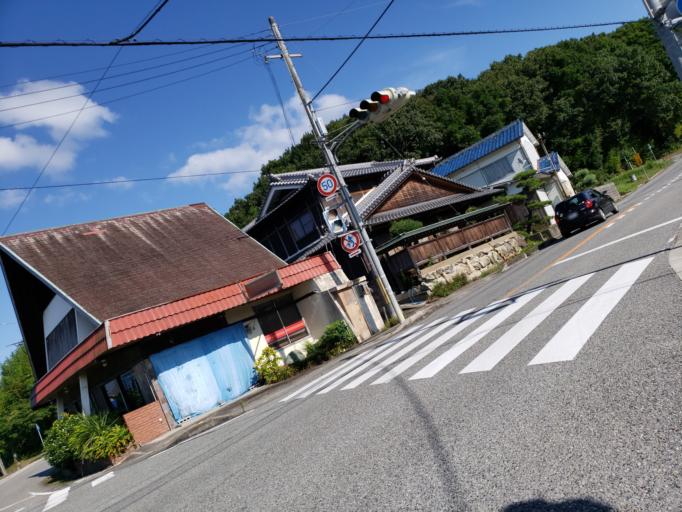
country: JP
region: Hyogo
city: Kakogawacho-honmachi
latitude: 34.8952
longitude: 134.8067
